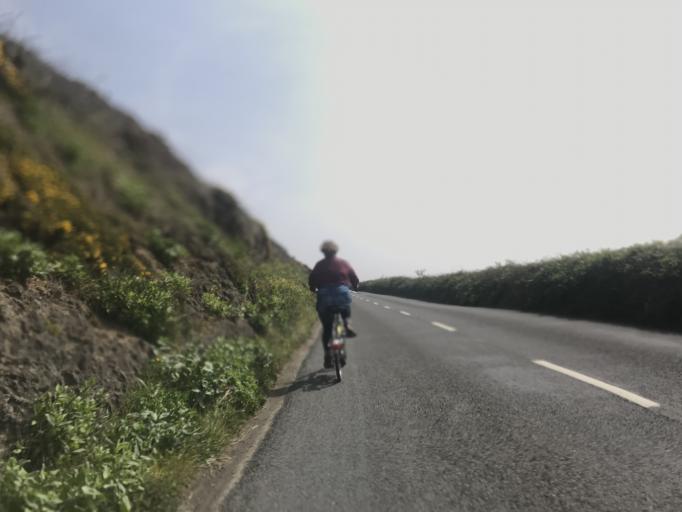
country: GB
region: England
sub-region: Devon
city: Braunton
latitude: 51.1213
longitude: -4.2373
